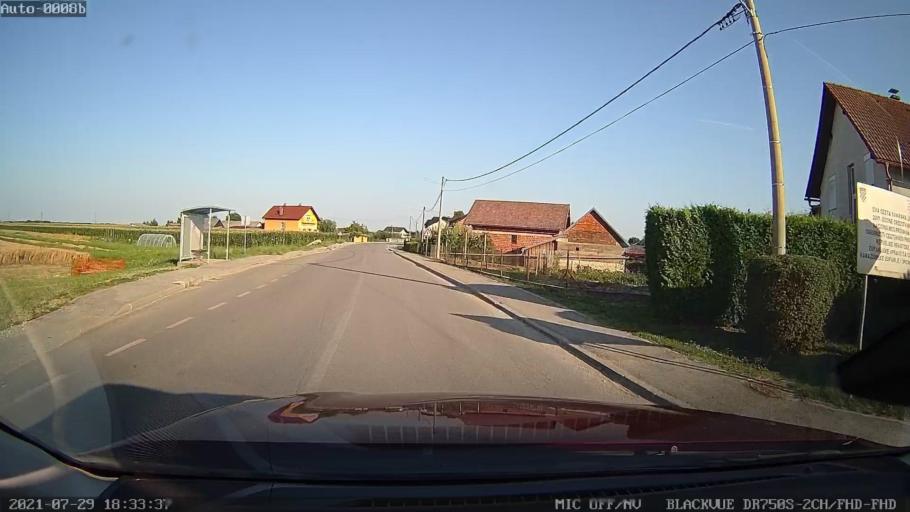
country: HR
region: Varazdinska
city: Vinica
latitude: 46.3148
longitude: 16.1591
